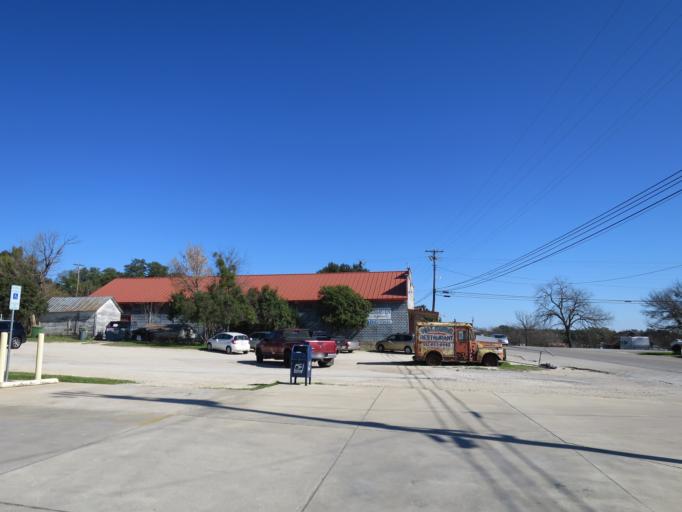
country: US
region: Texas
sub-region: Williamson County
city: Serenada
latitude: 30.7349
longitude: -97.5882
